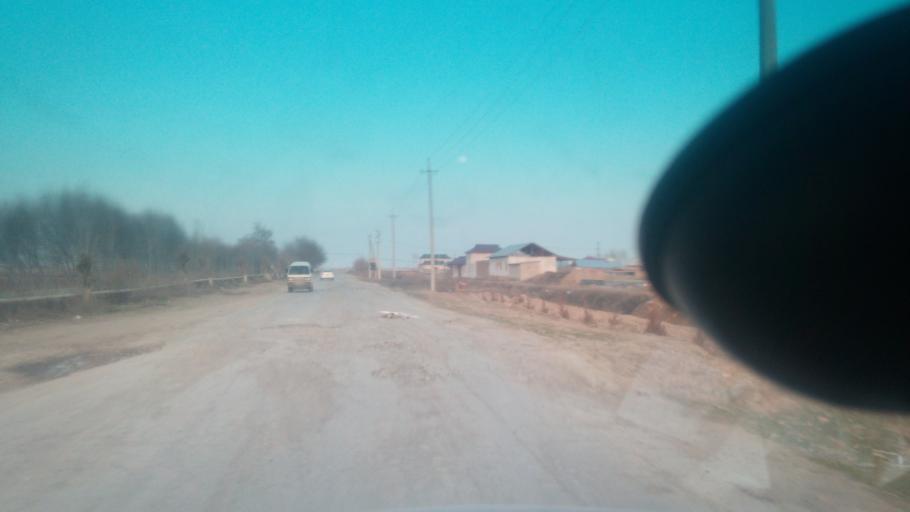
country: UZ
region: Sirdaryo
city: Guliston
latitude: 40.5261
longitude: 68.7845
